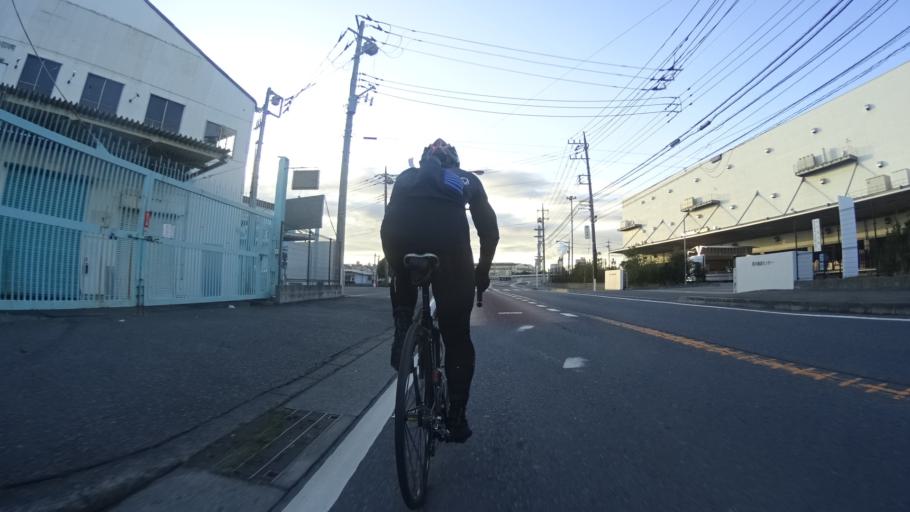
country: JP
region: Kanagawa
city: Atsugi
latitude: 35.4552
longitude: 139.3688
